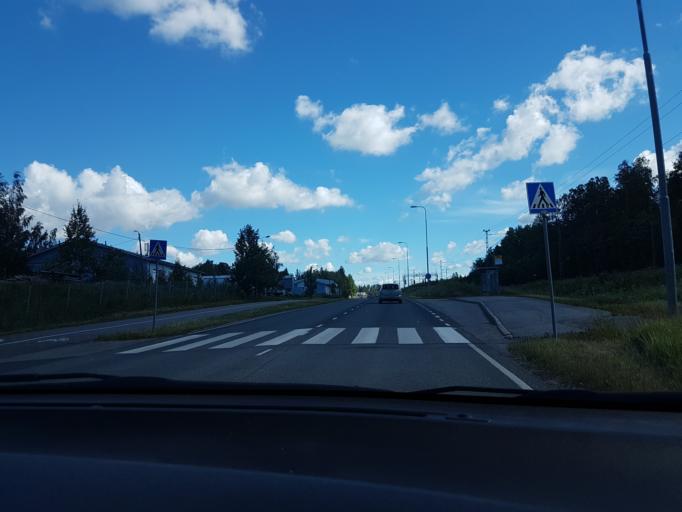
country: FI
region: Uusimaa
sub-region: Helsinki
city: Kerava
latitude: 60.3687
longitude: 25.0911
